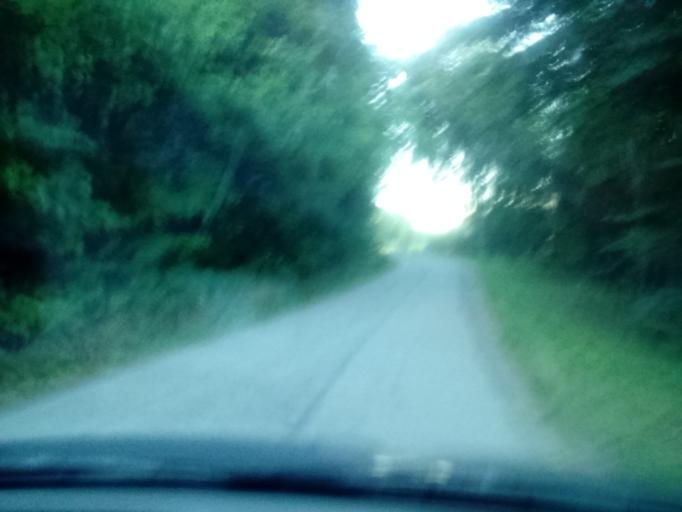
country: SE
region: Kalmar
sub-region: Vasterviks Kommun
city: Ankarsrum
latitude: 57.8078
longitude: 16.1628
